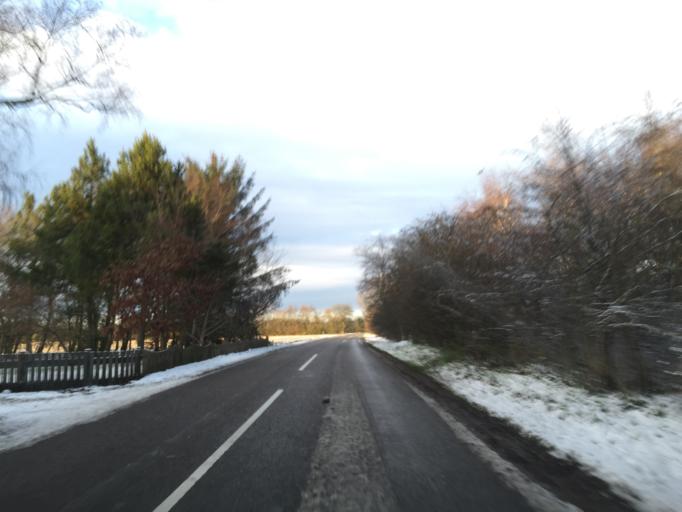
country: DK
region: Central Jutland
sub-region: Silkeborg Kommune
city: Svejbaek
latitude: 56.2355
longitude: 9.6804
